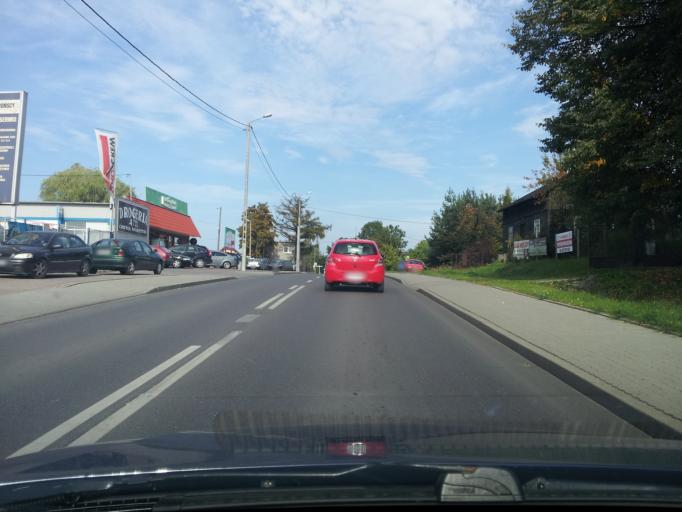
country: PL
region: Kujawsko-Pomorskie
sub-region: Powiat rypinski
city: Rypin
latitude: 53.0716
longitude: 19.4112
